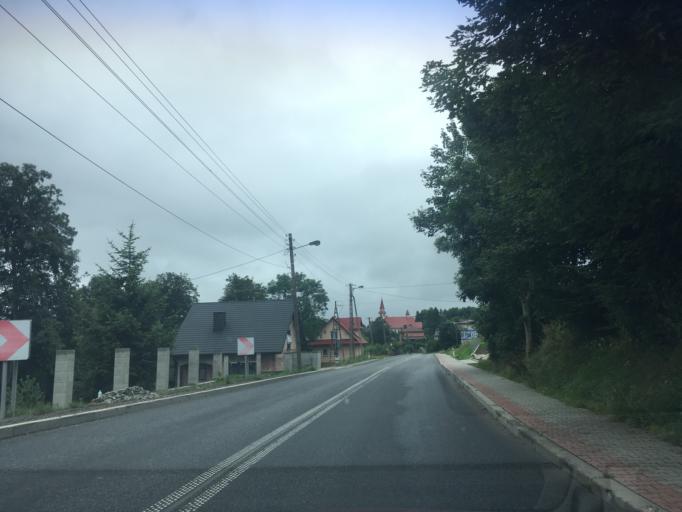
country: PL
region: Lesser Poland Voivodeship
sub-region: Powiat nowotarski
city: Rokiciny
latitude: 49.5915
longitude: 19.9231
